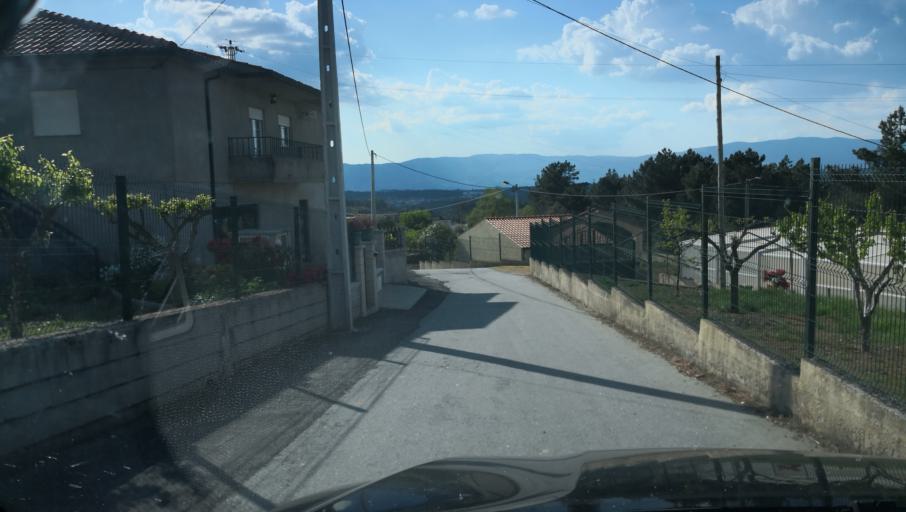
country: PT
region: Vila Real
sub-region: Sabrosa
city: Vilela
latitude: 41.2544
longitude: -7.6610
